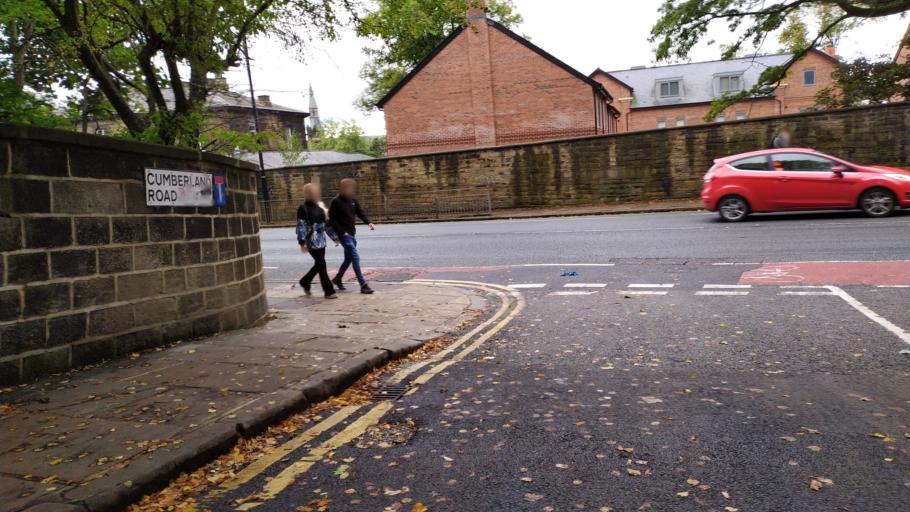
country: GB
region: England
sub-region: City and Borough of Leeds
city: Leeds
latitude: 53.8161
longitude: -1.5652
